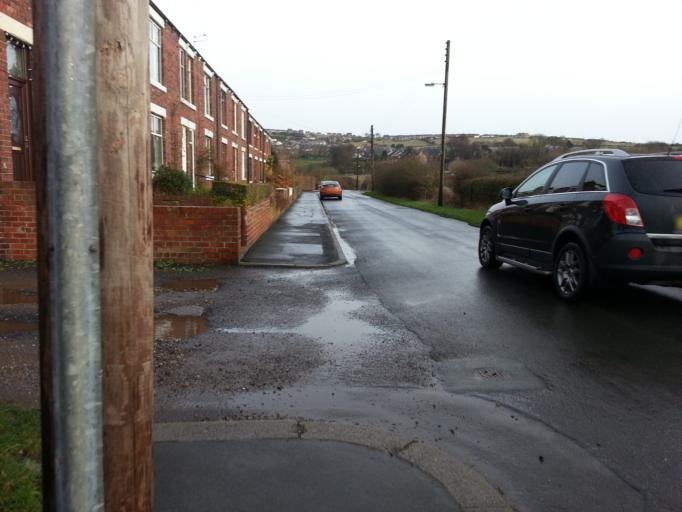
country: GB
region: England
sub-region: County Durham
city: Crook
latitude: 54.7268
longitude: -1.7573
